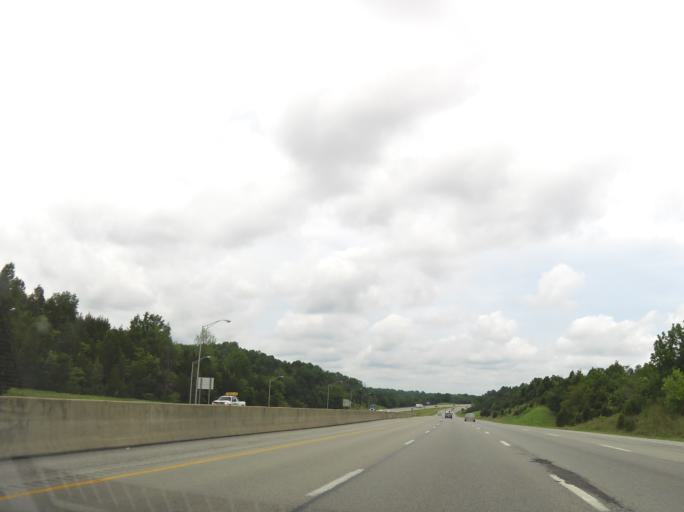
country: US
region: Kentucky
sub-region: Scott County
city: Georgetown
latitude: 38.3821
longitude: -84.5714
